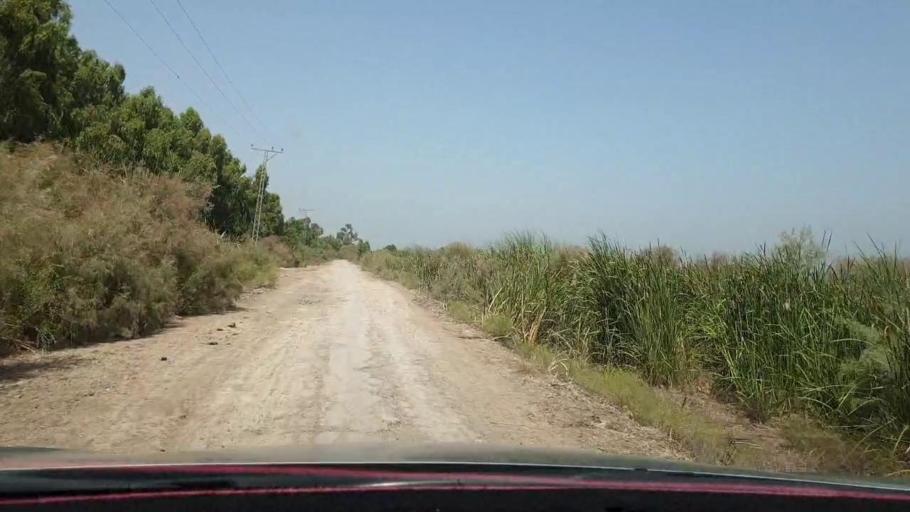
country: PK
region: Sindh
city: Warah
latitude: 27.4258
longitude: 67.6986
